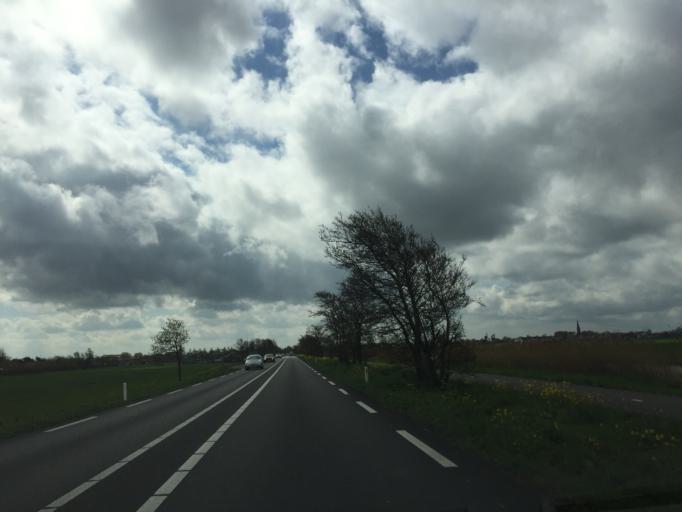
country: NL
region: South Holland
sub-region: Gemeente Rijnwoude
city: Benthuizen
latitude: 52.1071
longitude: 4.5889
